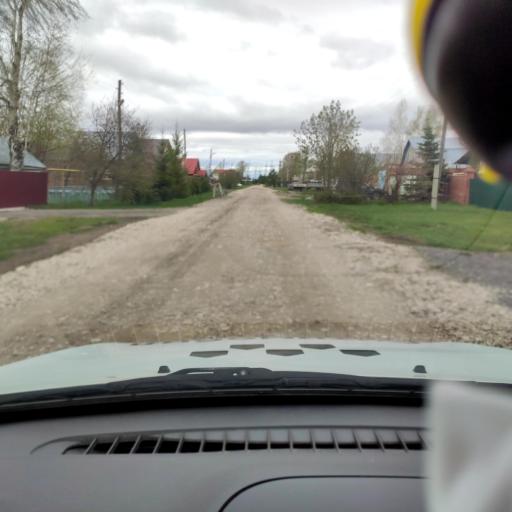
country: RU
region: Samara
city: Tol'yatti
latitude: 53.5812
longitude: 49.3300
